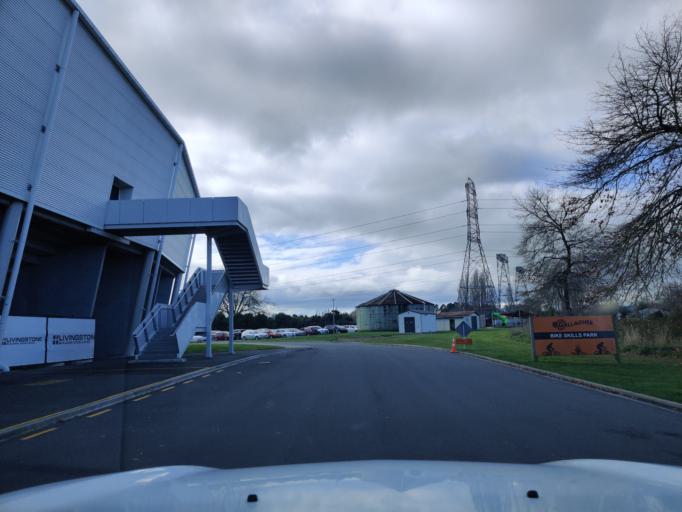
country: NZ
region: Waikato
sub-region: Waipa District
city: Cambridge
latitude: -37.8901
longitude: 175.4353
